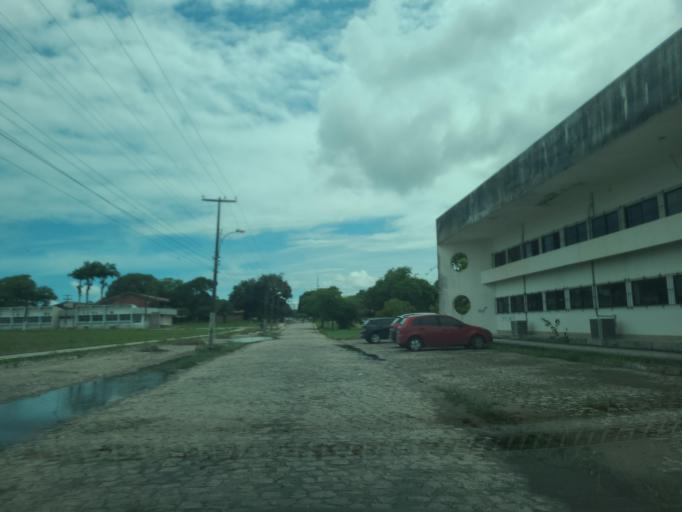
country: BR
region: Alagoas
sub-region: Satuba
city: Satuba
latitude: -9.5552
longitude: -35.7739
